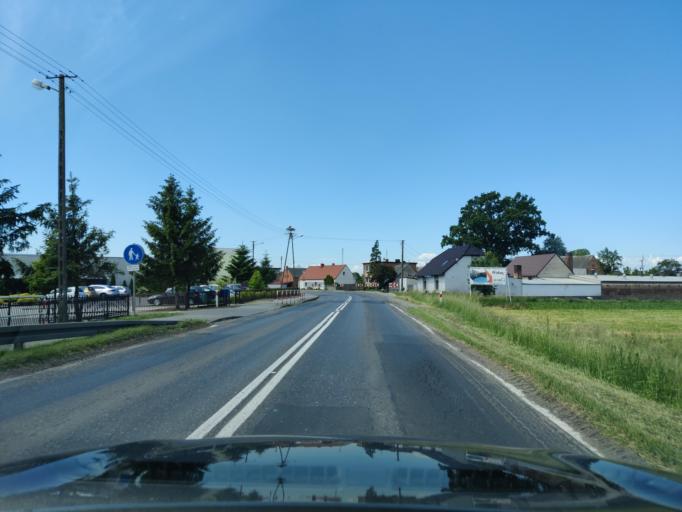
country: PL
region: Greater Poland Voivodeship
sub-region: Powiat grodziski
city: Grodzisk Wielkopolski
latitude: 52.1847
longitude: 16.3379
